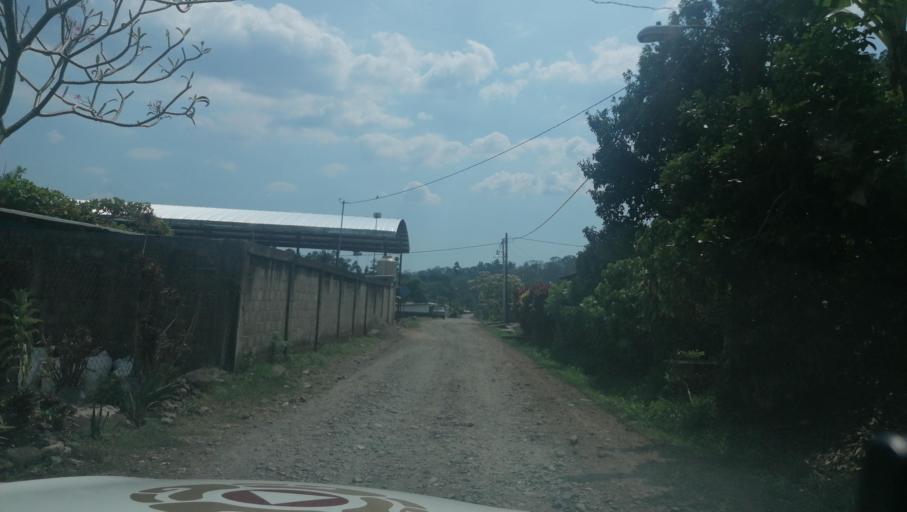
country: MX
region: Chiapas
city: Veinte de Noviembre
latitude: 15.0203
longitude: -92.2399
